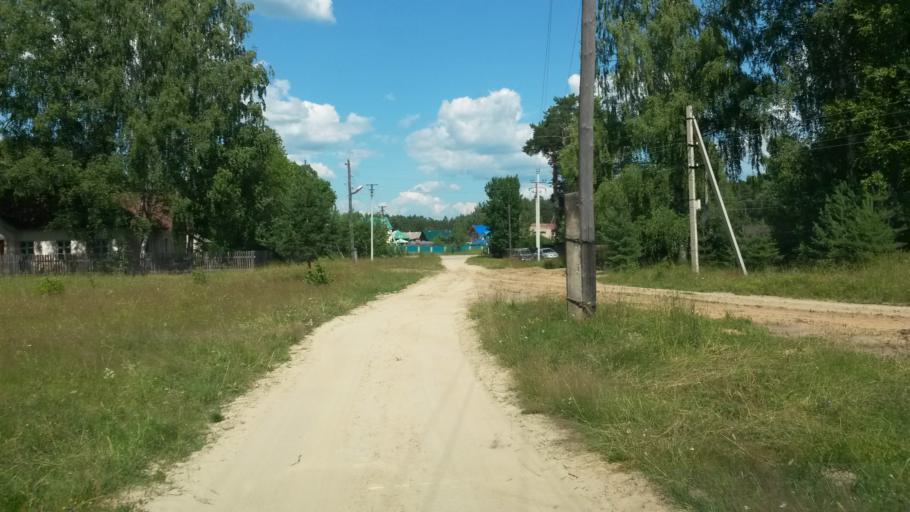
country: RU
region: Ivanovo
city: Zarechnyy
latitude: 57.4989
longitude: 42.3308
